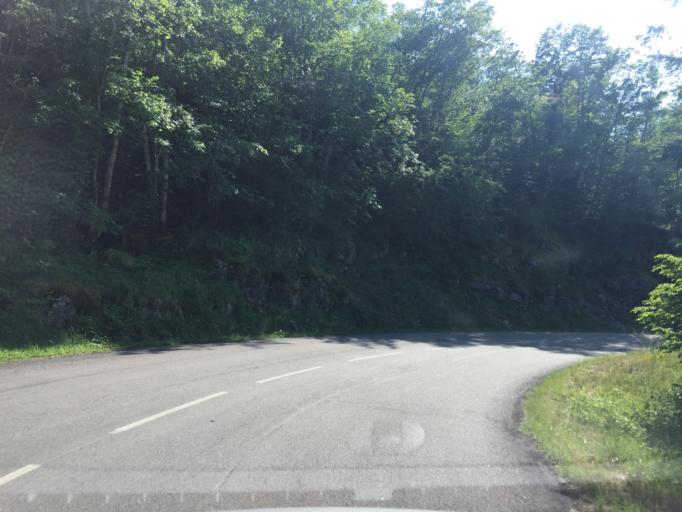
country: FR
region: Rhone-Alpes
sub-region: Departement de la Drome
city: Saint-Laurent-en-Royans
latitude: 45.0301
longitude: 5.3533
